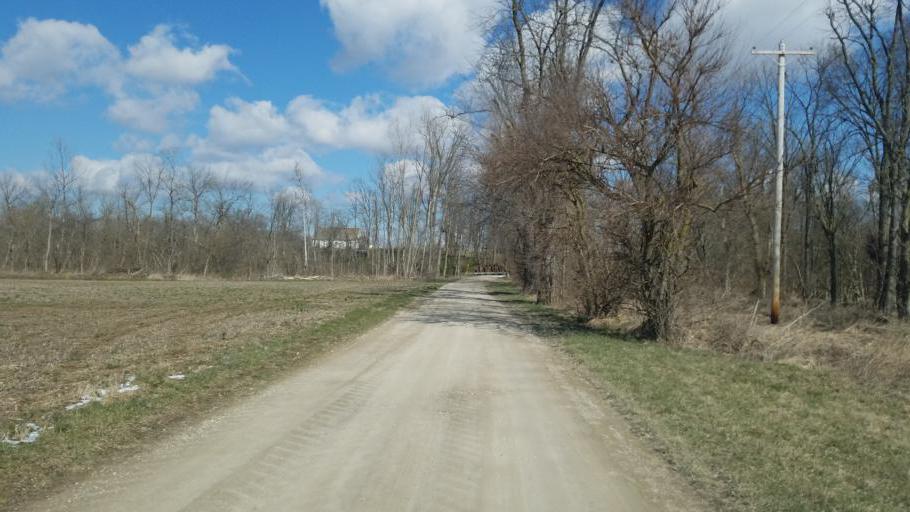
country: US
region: Ohio
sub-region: Licking County
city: Utica
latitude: 40.2526
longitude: -82.5080
